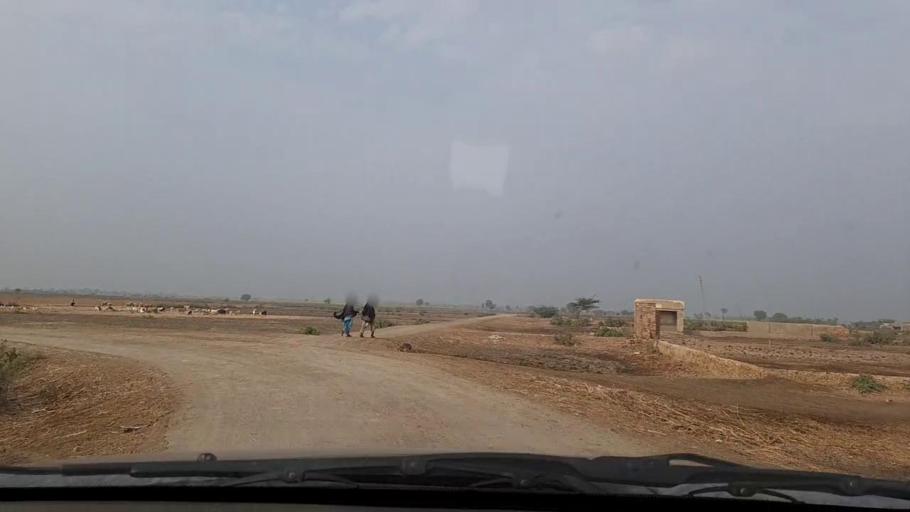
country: PK
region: Sindh
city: Pithoro
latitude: 25.7606
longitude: 69.4055
